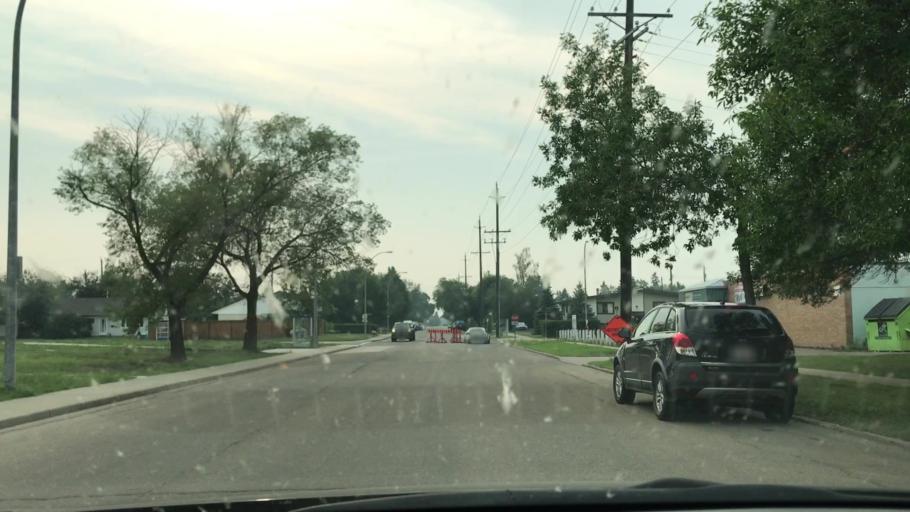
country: CA
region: Alberta
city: Edmonton
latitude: 53.5922
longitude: -113.5476
